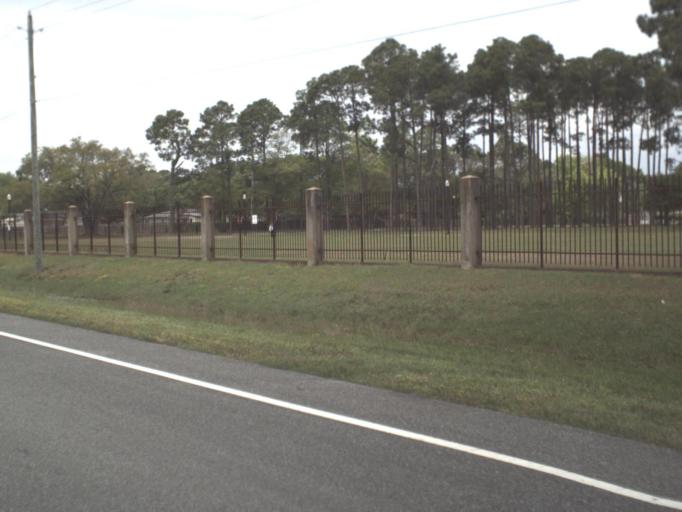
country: US
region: Florida
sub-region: Escambia County
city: Myrtle Grove
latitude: 30.3969
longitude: -87.2998
